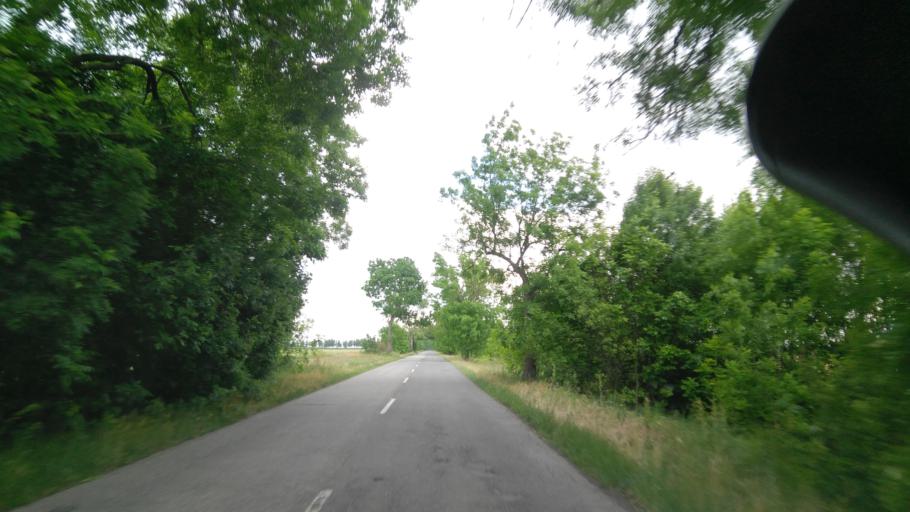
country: HU
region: Bekes
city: Bucsa
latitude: 47.1567
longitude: 21.1096
